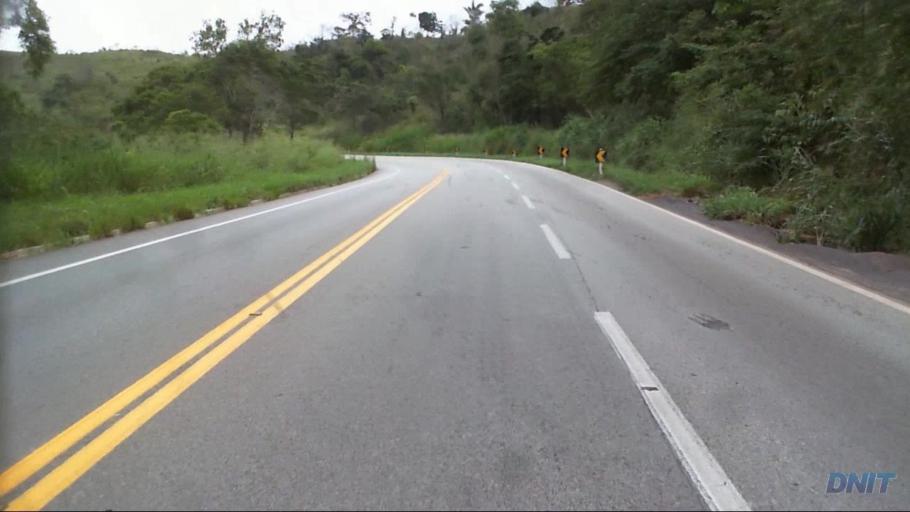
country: BR
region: Minas Gerais
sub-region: Nova Era
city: Nova Era
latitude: -19.7910
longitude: -43.0545
